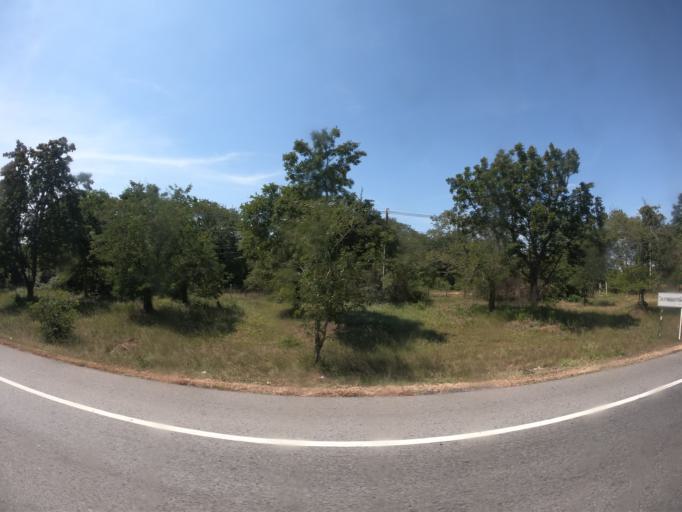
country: TH
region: Khon Kaen
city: Phon
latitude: 15.7715
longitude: 102.6066
